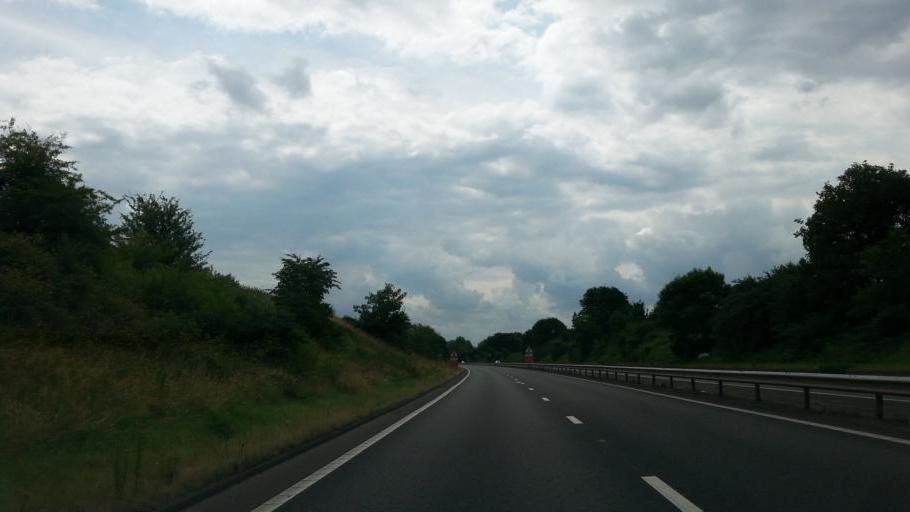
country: GB
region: England
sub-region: Warwickshire
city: Curdworth
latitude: 52.5371
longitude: -1.7783
